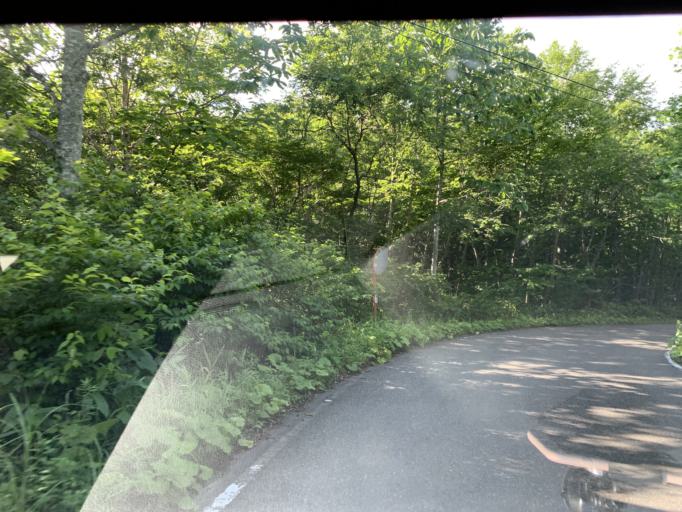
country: JP
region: Iwate
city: Ichinoseki
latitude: 38.9112
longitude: 140.8289
